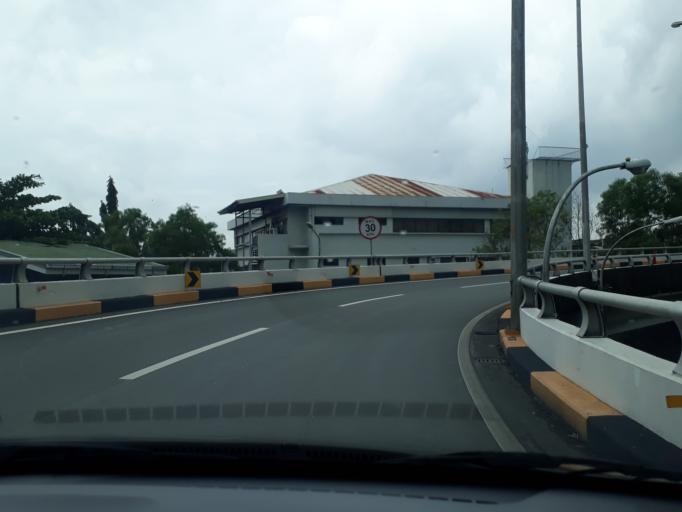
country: PH
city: Sambayanihan People's Village
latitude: 14.4853
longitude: 121.0423
